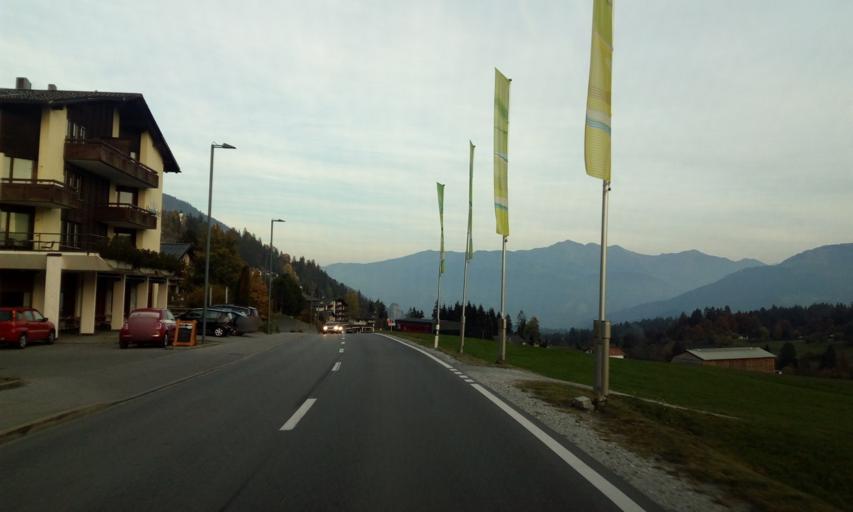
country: CH
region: Grisons
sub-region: Imboden District
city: Flims
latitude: 46.8365
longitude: 9.2901
